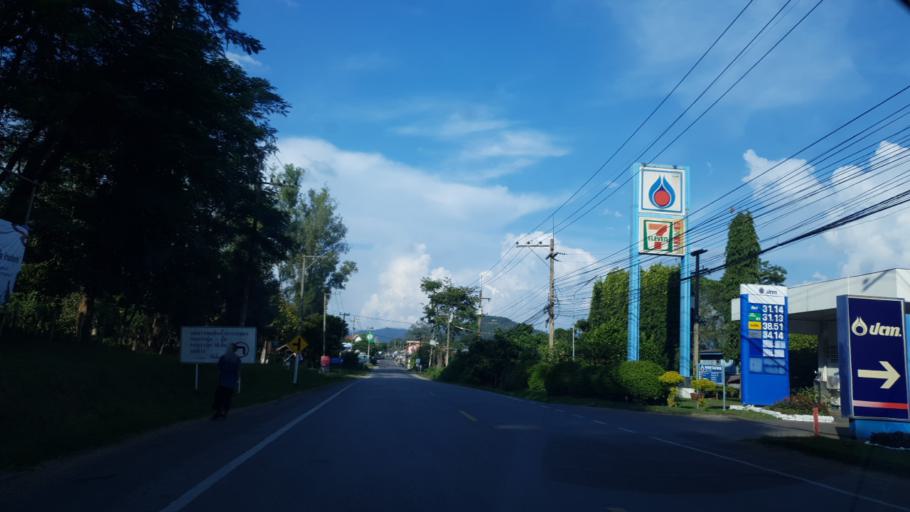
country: TH
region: Mae Hong Son
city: Khun Yuam
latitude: 18.8124
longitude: 97.9334
